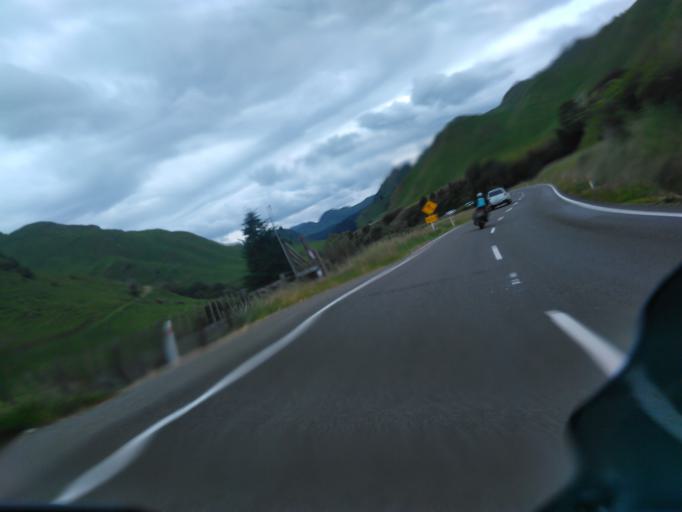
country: NZ
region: Bay of Plenty
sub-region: Opotiki District
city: Opotiki
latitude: -38.3655
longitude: 177.4627
